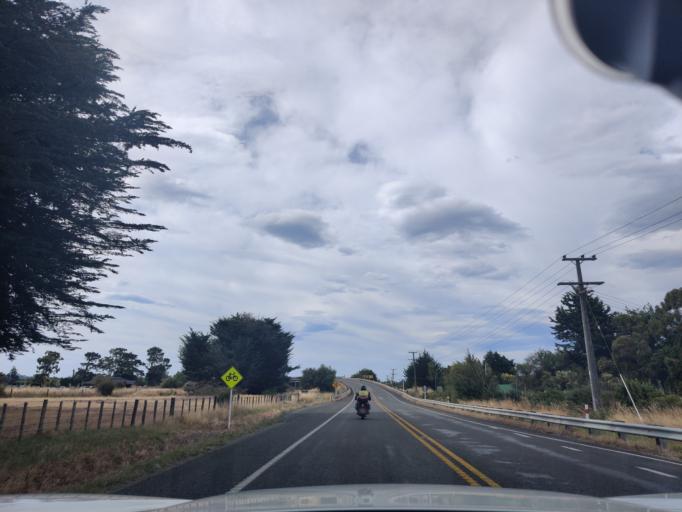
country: NZ
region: Wellington
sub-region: Masterton District
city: Masterton
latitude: -40.8929
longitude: 175.6613
